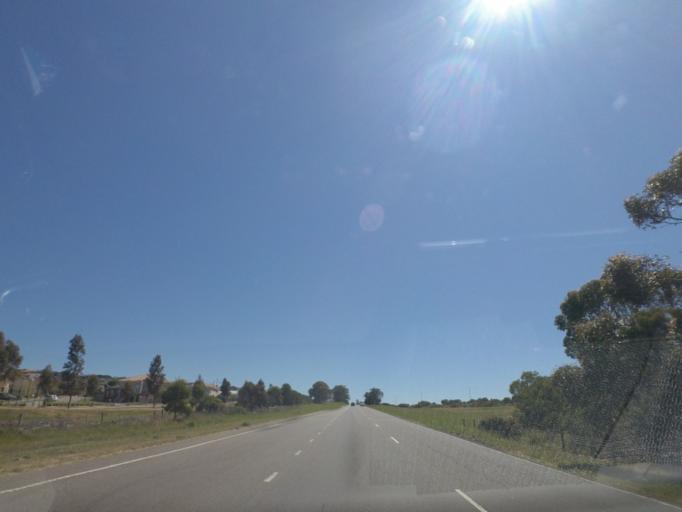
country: AU
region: Victoria
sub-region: Hume
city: Craigieburn
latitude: -37.5752
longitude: 144.9395
